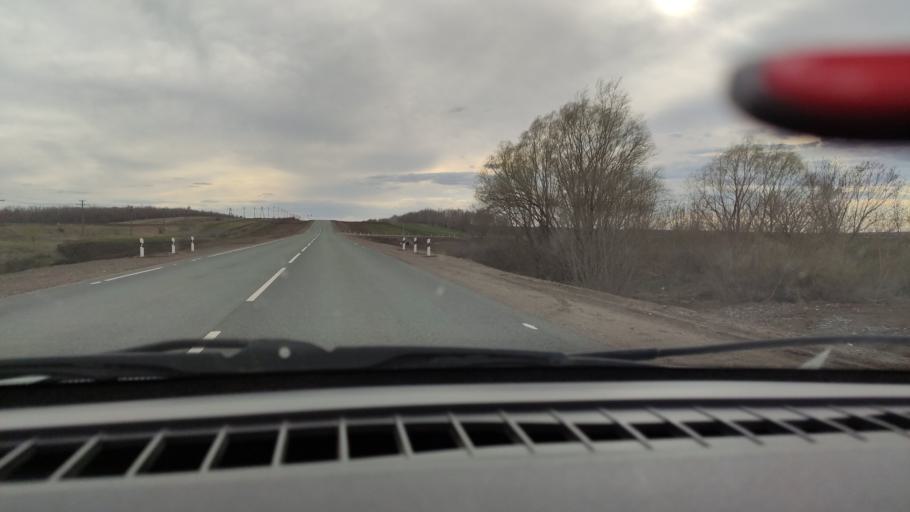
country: RU
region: Bashkortostan
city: Mayachnyy
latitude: 52.3518
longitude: 55.5640
